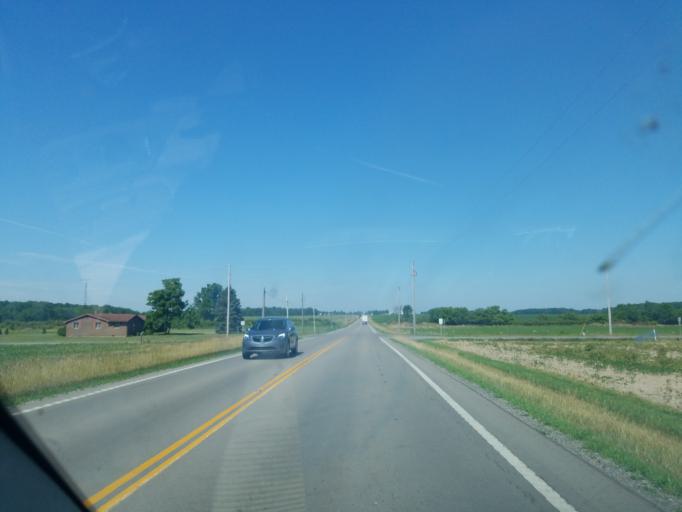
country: US
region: Ohio
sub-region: Shelby County
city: Jackson Center
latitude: 40.4393
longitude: -83.9928
